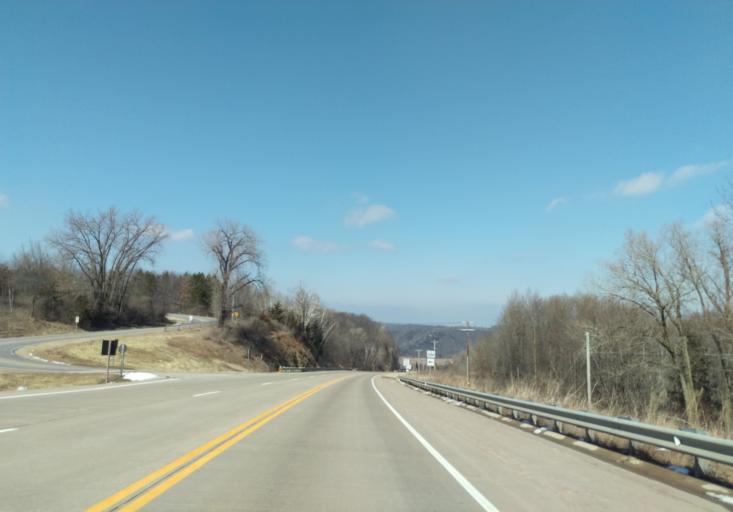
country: US
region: Wisconsin
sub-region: La Crosse County
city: La Crosse
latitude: 43.7384
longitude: -91.1108
